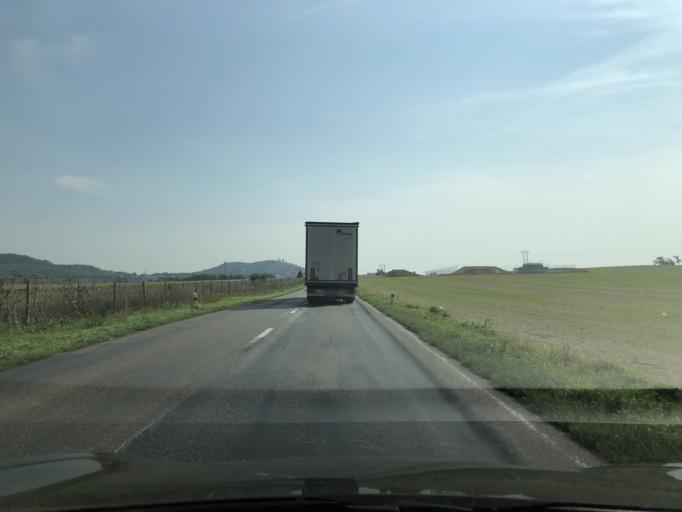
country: CZ
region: South Moravian
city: Brezi
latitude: 48.8146
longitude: 16.6020
